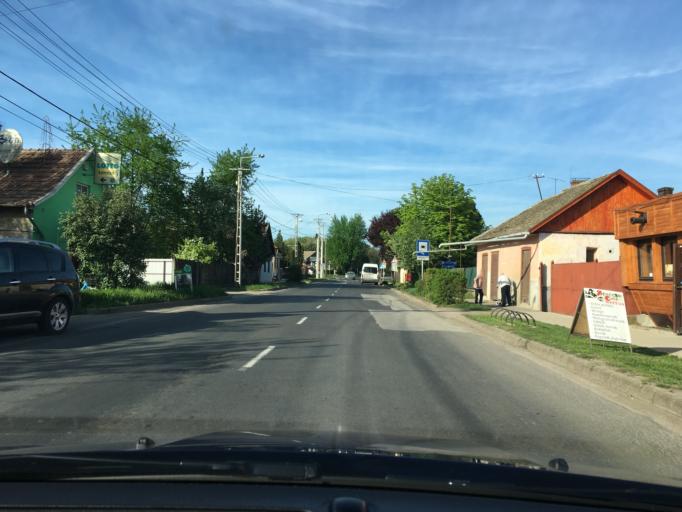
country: HU
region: Bekes
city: Korostarcsa
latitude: 46.8804
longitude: 21.0268
